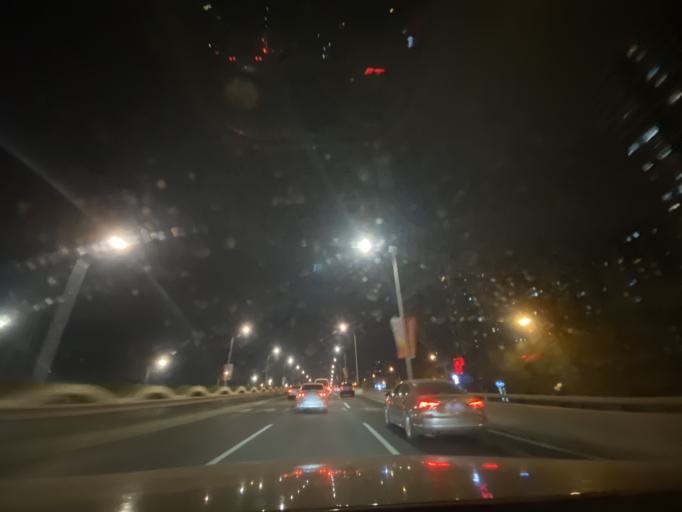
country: CN
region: Beijing
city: Babaoshan
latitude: 39.8958
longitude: 116.2325
